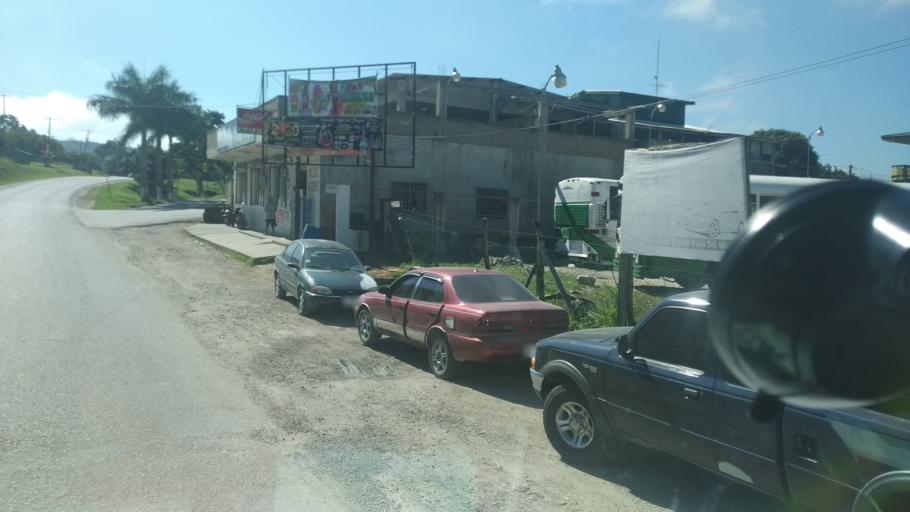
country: BZ
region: Cayo
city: Benque Viejo del Carmen
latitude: 17.0788
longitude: -89.1368
